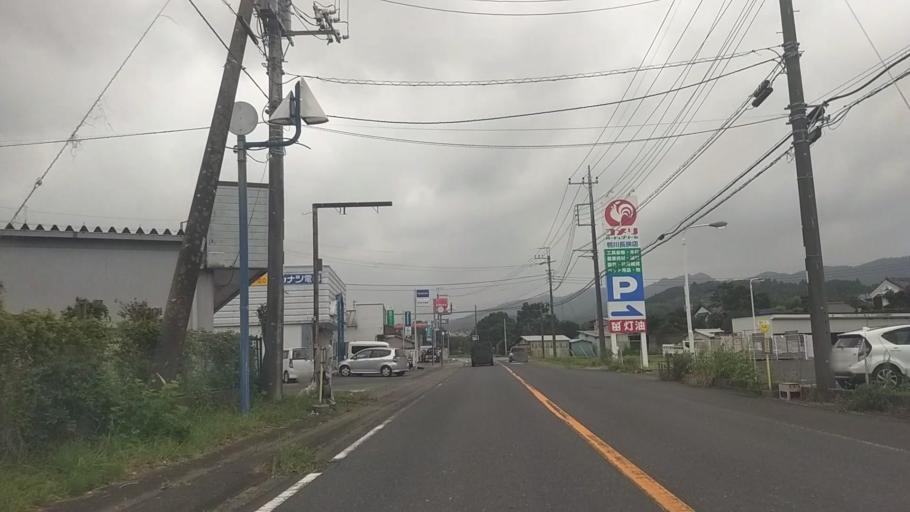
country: JP
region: Chiba
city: Kawaguchi
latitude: 35.1347
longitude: 140.0037
